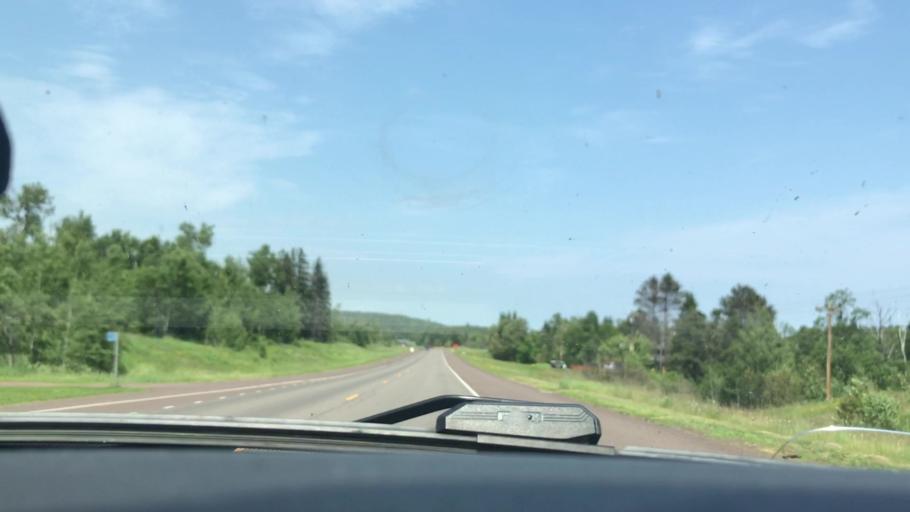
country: US
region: Minnesota
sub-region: Lake County
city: Silver Bay
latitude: 47.3237
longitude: -91.2148
